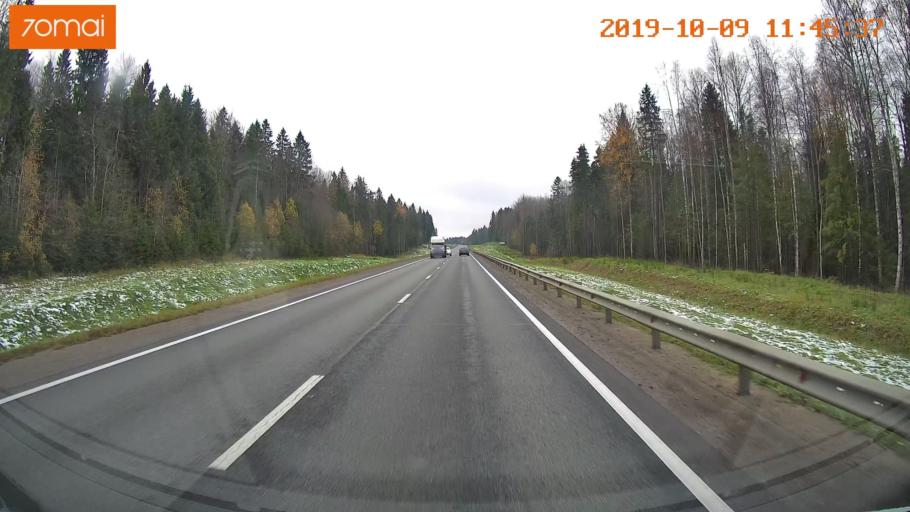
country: RU
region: Vologda
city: Gryazovets
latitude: 58.8662
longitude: 40.1978
